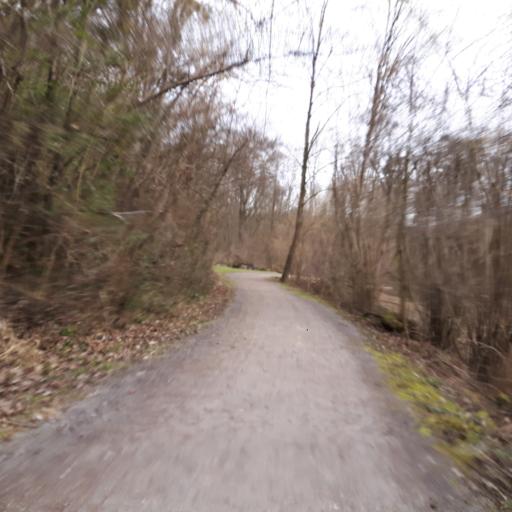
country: DE
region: Baden-Wuerttemberg
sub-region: Regierungsbezirk Stuttgart
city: Neckarwestheim
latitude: 49.0596
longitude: 9.2100
